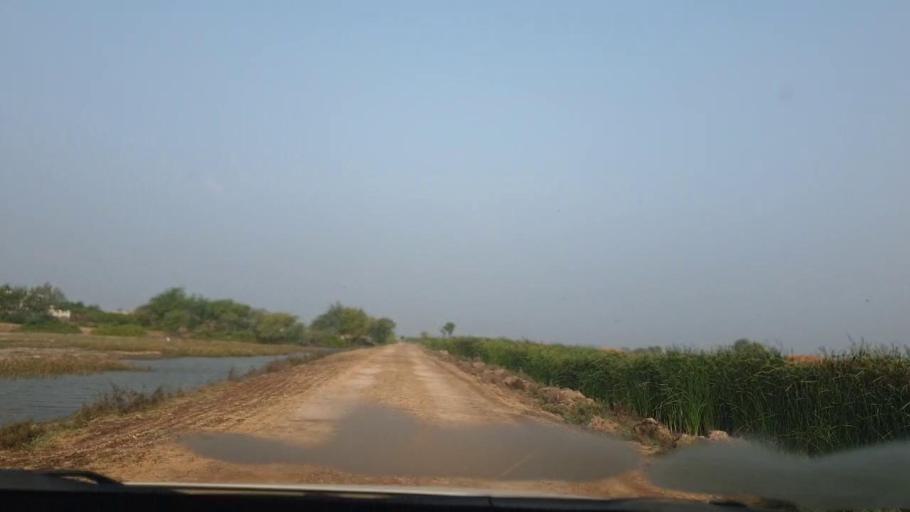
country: PK
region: Sindh
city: Tando Muhammad Khan
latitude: 25.0916
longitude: 68.4796
